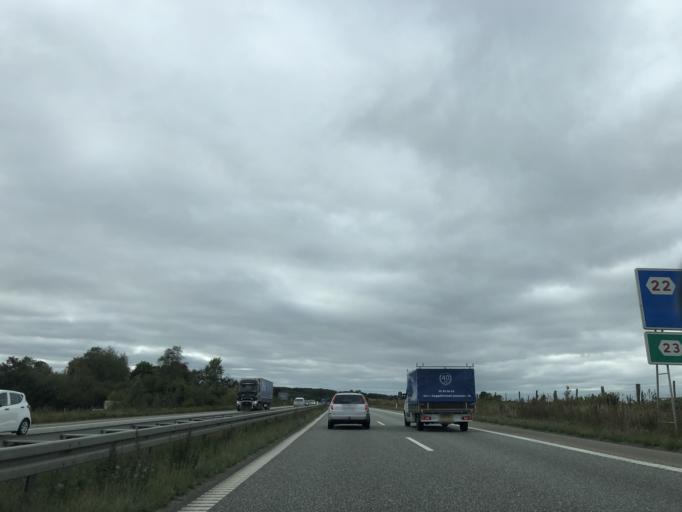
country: DK
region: Central Jutland
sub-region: Arhus Kommune
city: Framlev
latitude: 56.1529
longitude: 9.9902
